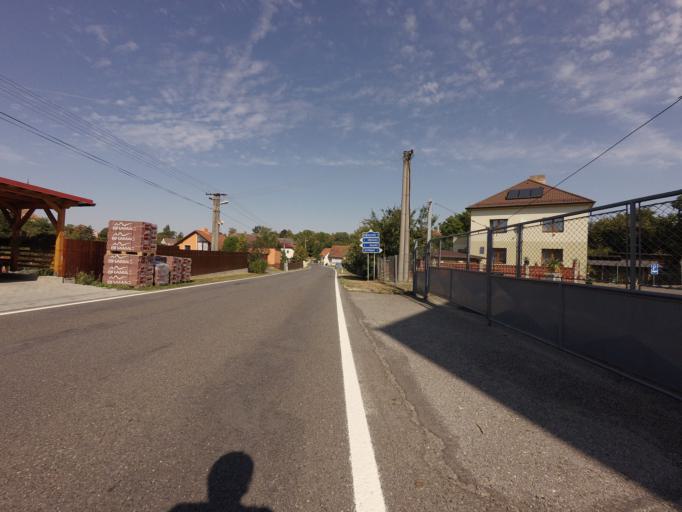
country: CZ
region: Jihocesky
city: Bernartice
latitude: 49.3873
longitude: 14.3589
